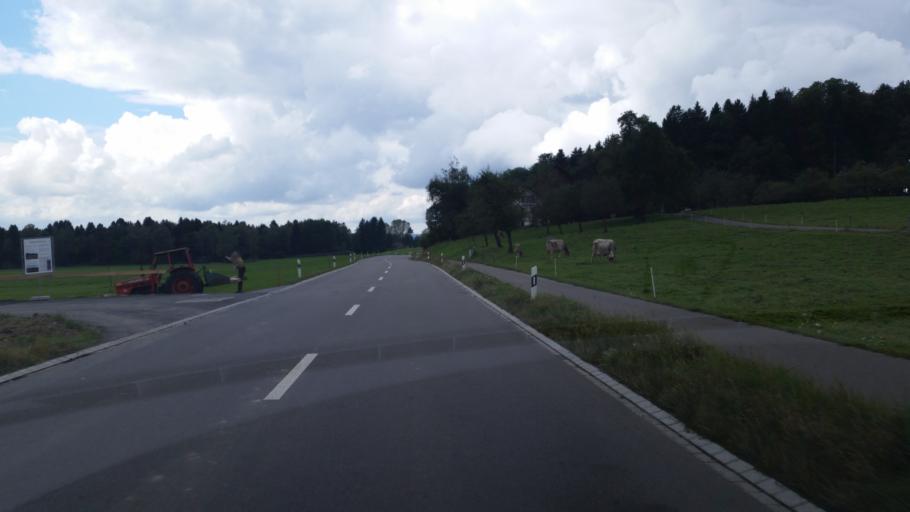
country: CH
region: Zurich
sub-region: Bezirk Affoltern
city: Hausen am Albis / Hausen (Dorf)
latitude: 47.2435
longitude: 8.5201
